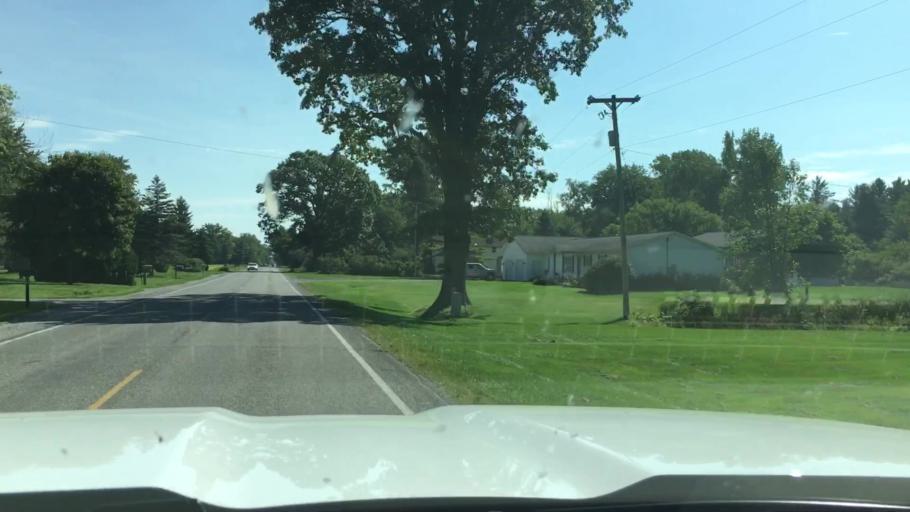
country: US
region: Michigan
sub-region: Saginaw County
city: Freeland
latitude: 43.5252
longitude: -84.1571
